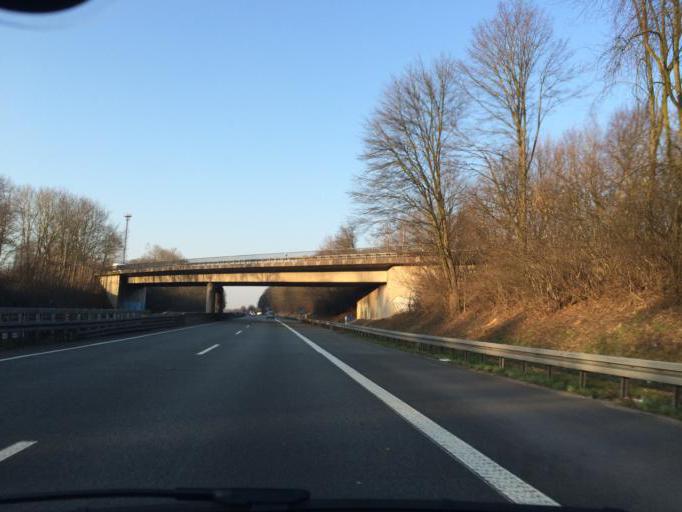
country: DE
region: North Rhine-Westphalia
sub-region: Regierungsbezirk Munster
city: Haltern
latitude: 51.7641
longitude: 7.1744
